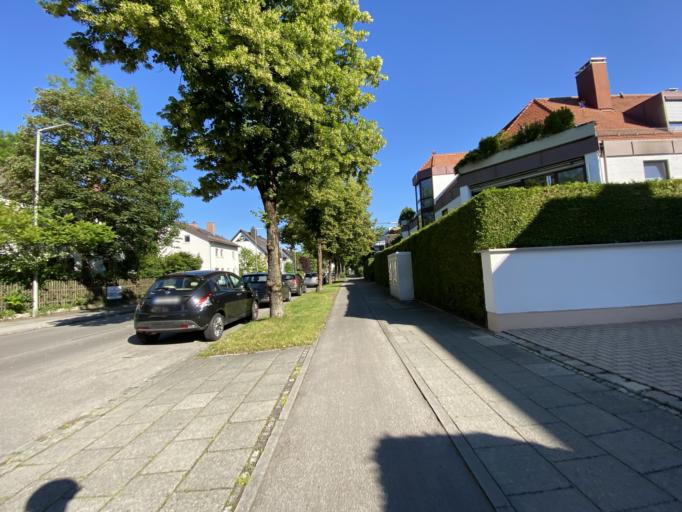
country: DE
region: Bavaria
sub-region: Upper Bavaria
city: Pasing
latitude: 48.1590
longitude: 11.4479
